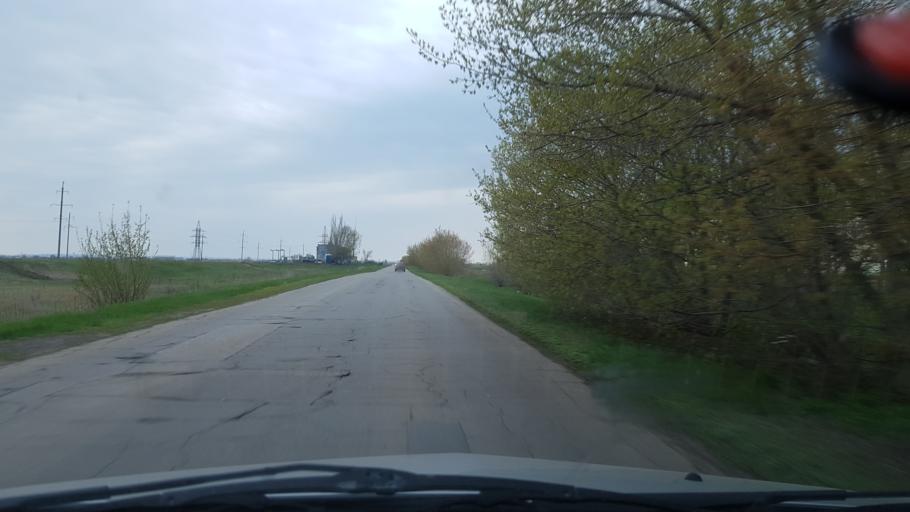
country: RU
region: Samara
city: Khryashchevka
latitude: 53.6703
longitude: 49.1130
